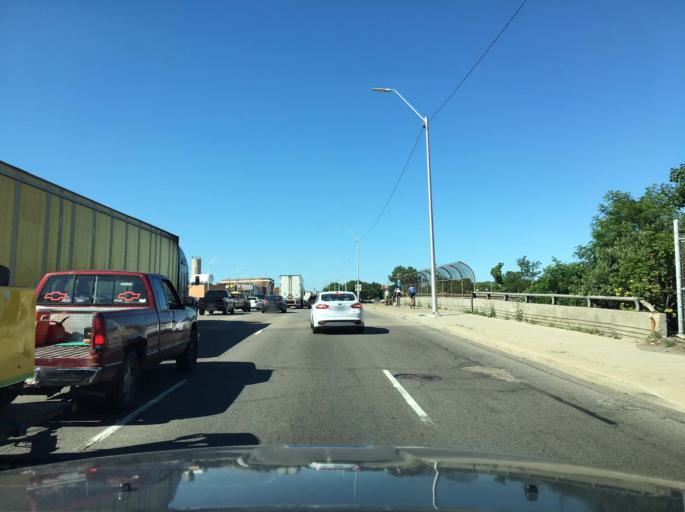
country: US
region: Michigan
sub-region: Wayne County
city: Detroit
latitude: 42.3467
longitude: -83.0361
